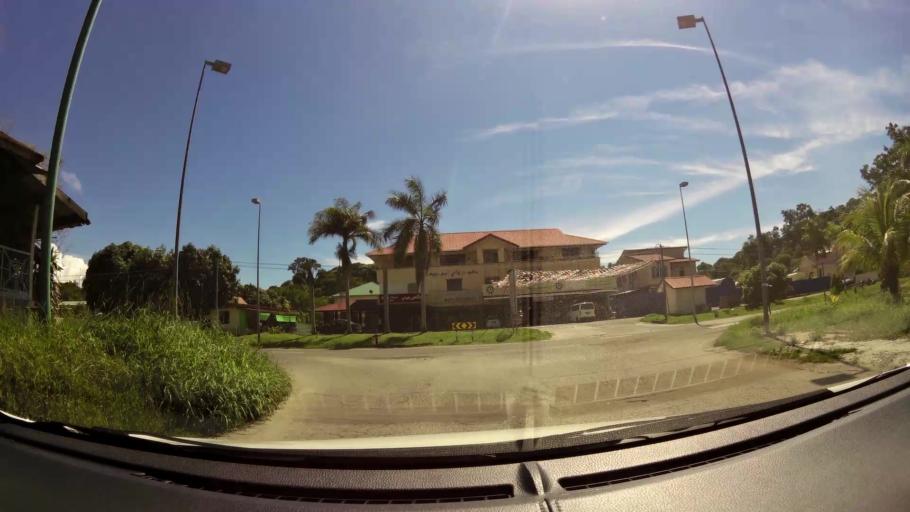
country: BN
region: Brunei and Muara
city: Bandar Seri Begawan
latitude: 5.0140
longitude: 115.0585
